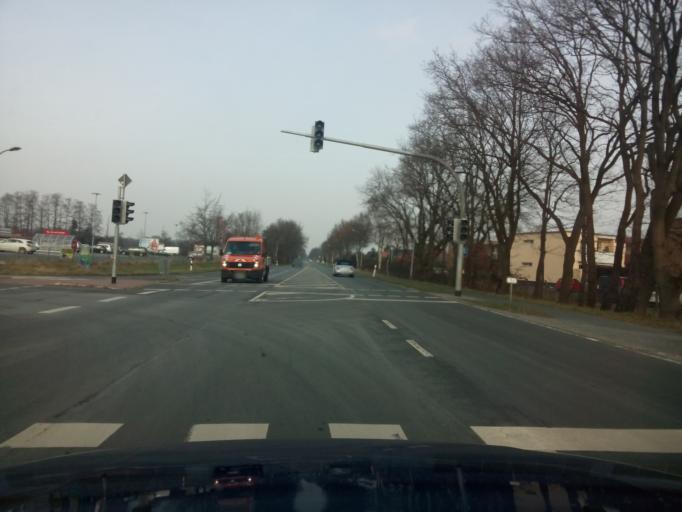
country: DE
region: Lower Saxony
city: Langen
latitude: 53.6164
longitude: 8.5978
